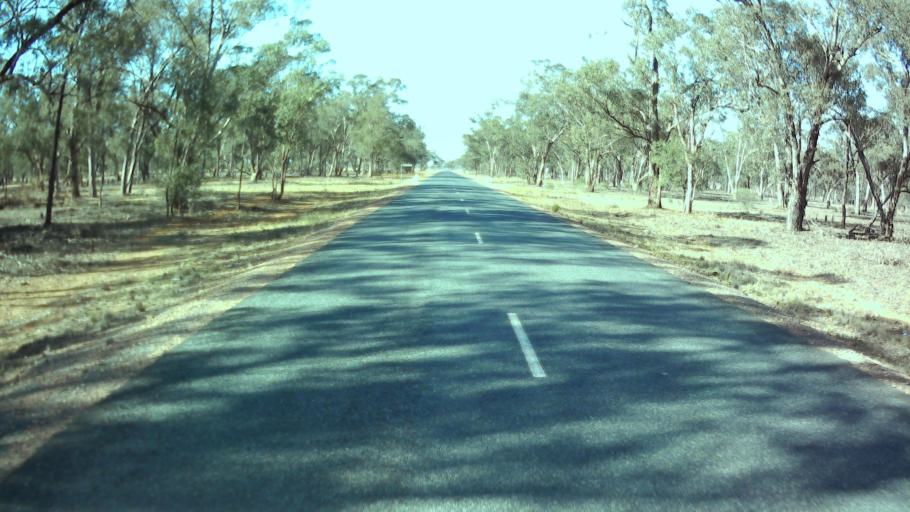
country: AU
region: New South Wales
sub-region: Weddin
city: Grenfell
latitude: -34.0640
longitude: 147.9081
